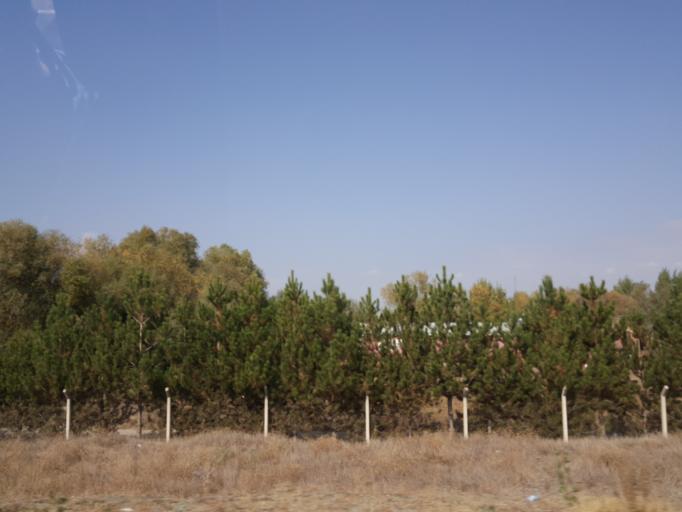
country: TR
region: Corum
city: Alaca
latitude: 40.1524
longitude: 34.8524
